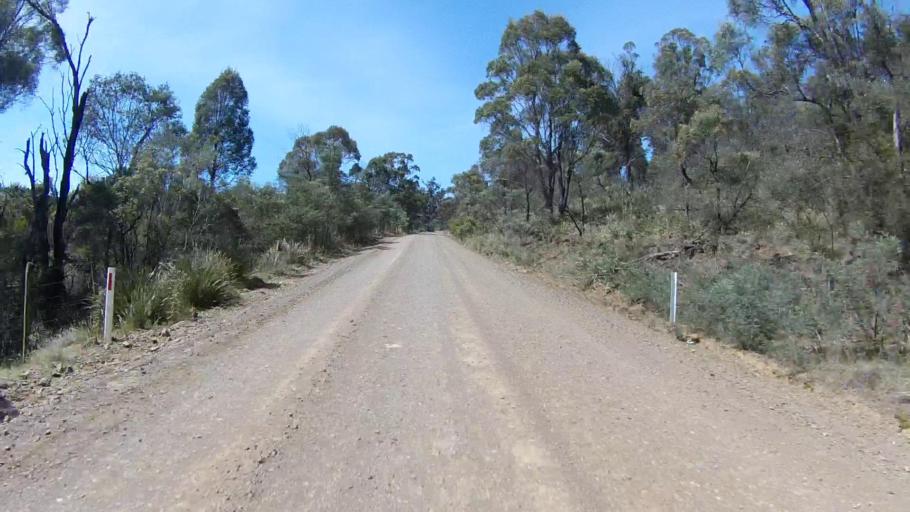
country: AU
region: Tasmania
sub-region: Sorell
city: Sorell
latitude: -42.6462
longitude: 147.7421
